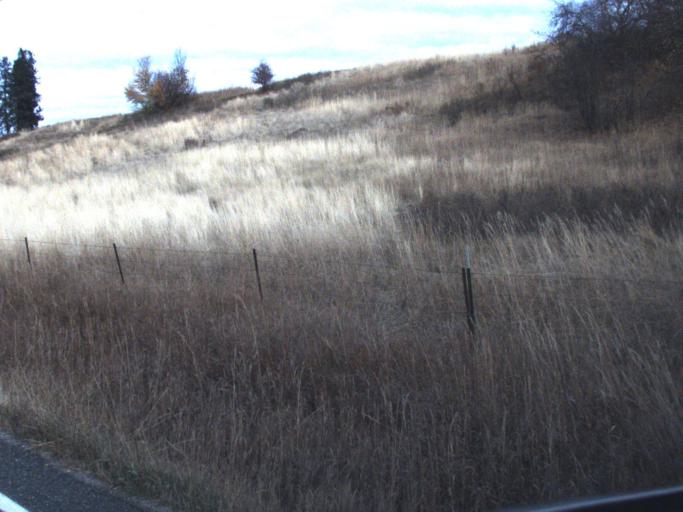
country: US
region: Washington
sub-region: Stevens County
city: Kettle Falls
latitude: 48.7417
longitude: -118.0488
